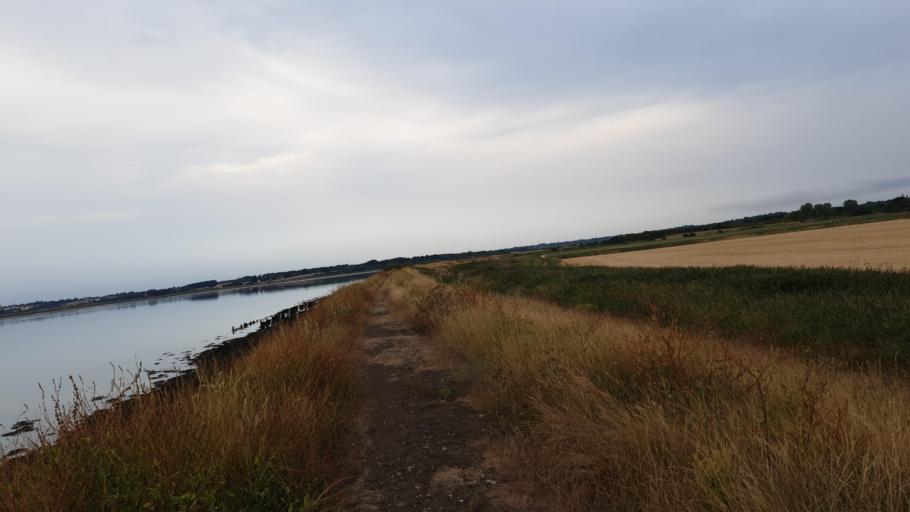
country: GB
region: England
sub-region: Essex
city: Brightlingsea
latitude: 51.8208
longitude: 0.9905
